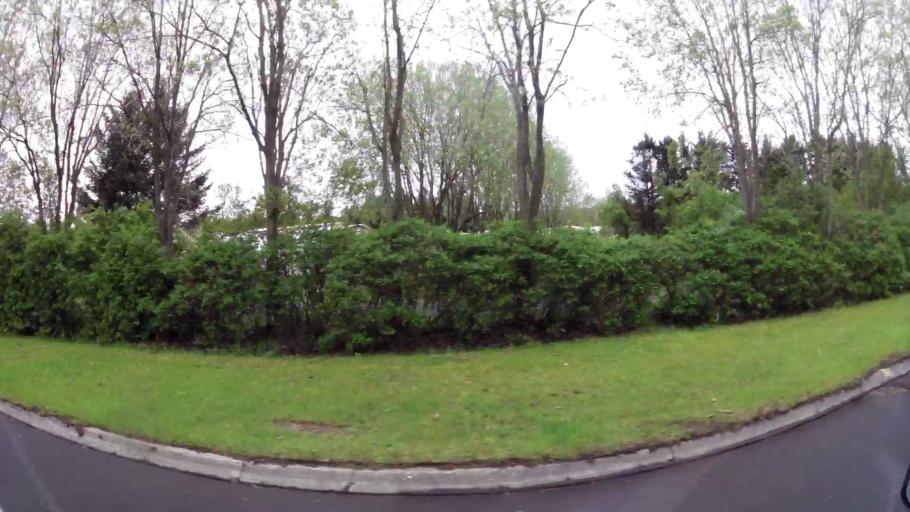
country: IS
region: Capital Region
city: Reykjavik
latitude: 64.1408
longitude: -21.8671
